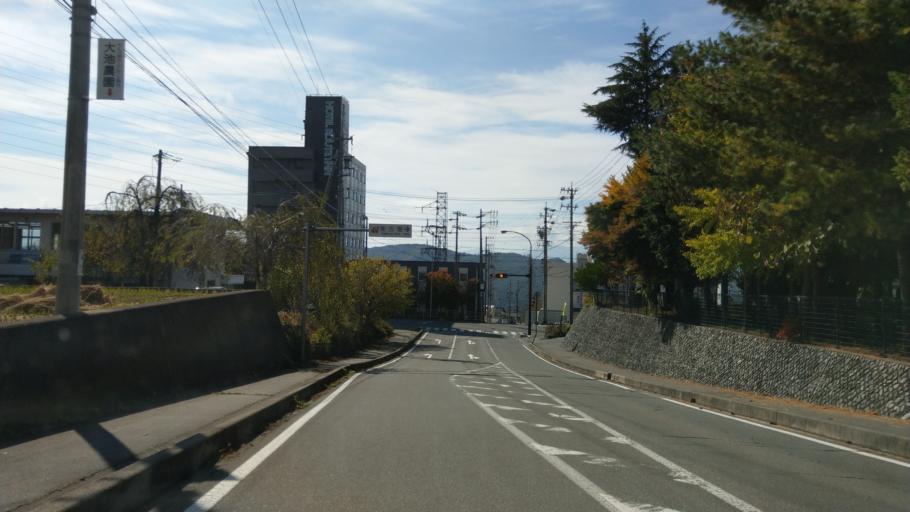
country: JP
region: Nagano
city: Komoro
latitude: 36.3294
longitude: 138.4341
